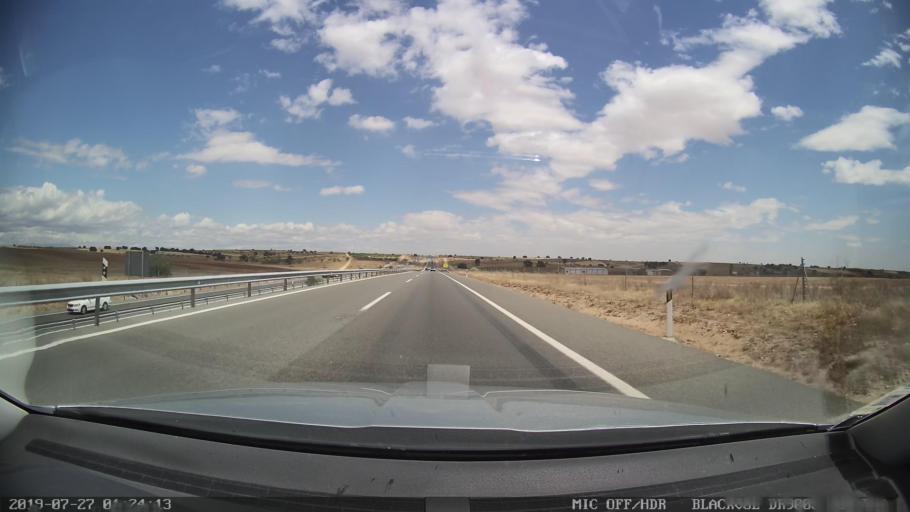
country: ES
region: Castille-La Mancha
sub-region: Province of Toledo
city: Santa Cruz del Retamar
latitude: 40.1286
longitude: -4.2132
